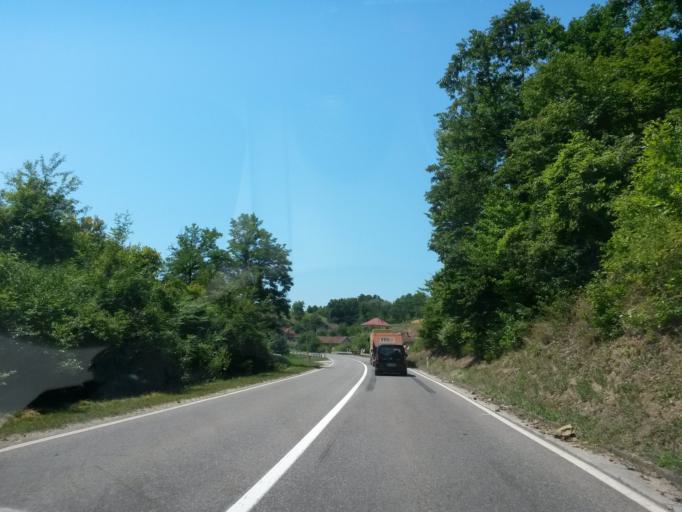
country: BA
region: Federation of Bosnia and Herzegovina
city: Odzak
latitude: 44.9426
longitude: 18.2072
